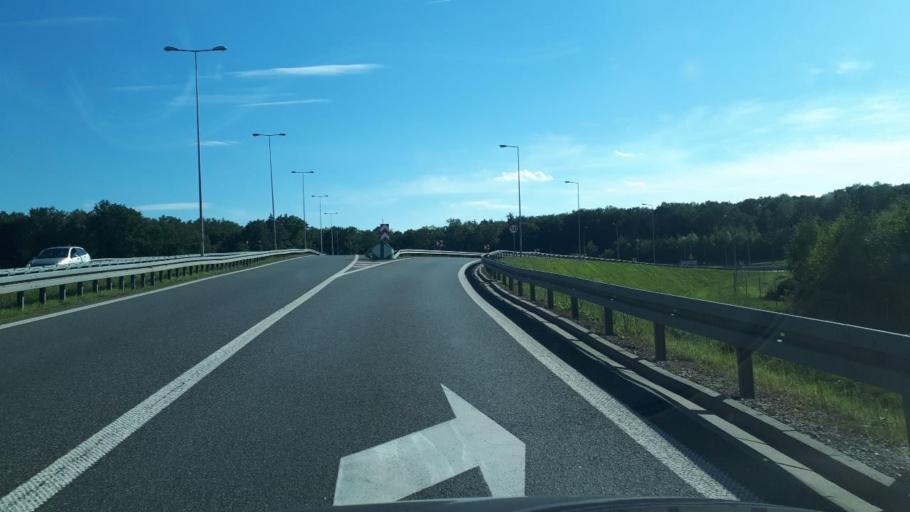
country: PL
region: Silesian Voivodeship
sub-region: Gliwice
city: Gliwice
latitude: 50.3091
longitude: 18.7218
